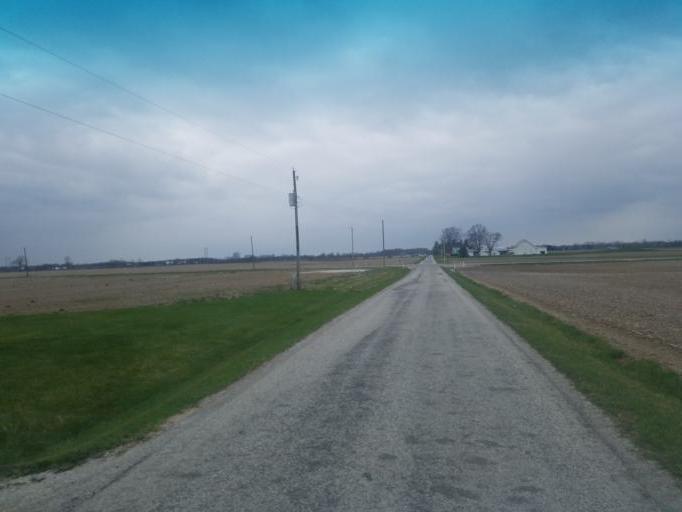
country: US
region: Ohio
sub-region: Marion County
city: Prospect
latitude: 40.4410
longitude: -83.1584
